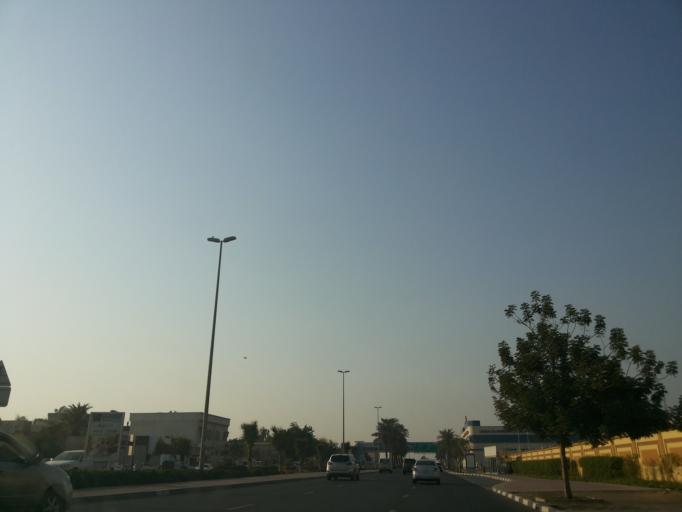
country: AE
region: Ash Shariqah
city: Sharjah
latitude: 25.2810
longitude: 55.3422
